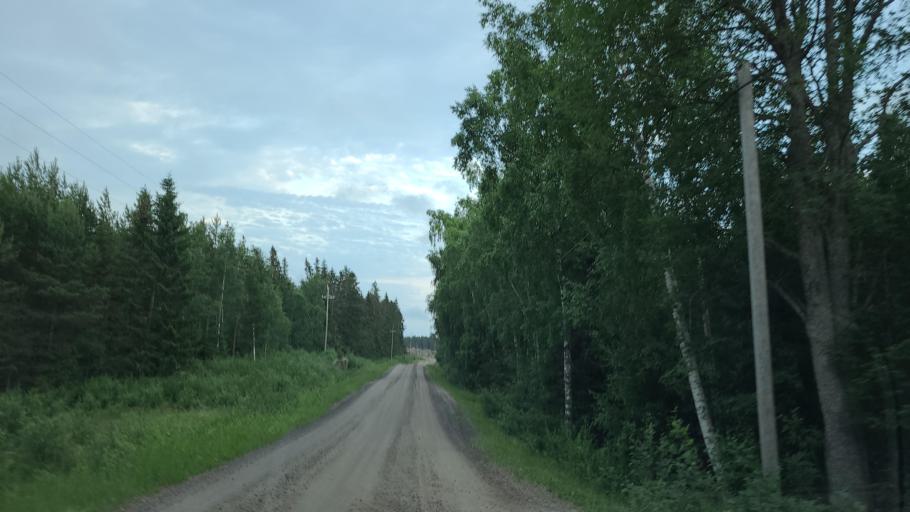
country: FI
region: Ostrobothnia
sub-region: Vaasa
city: Replot
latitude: 63.3212
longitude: 21.1437
